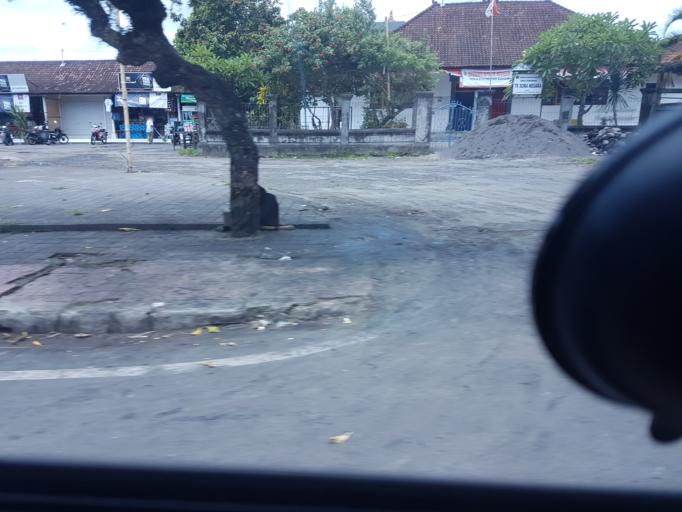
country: ID
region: Bali
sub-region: Kabupaten Gianyar
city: Ubud
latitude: -8.5138
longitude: 115.2934
